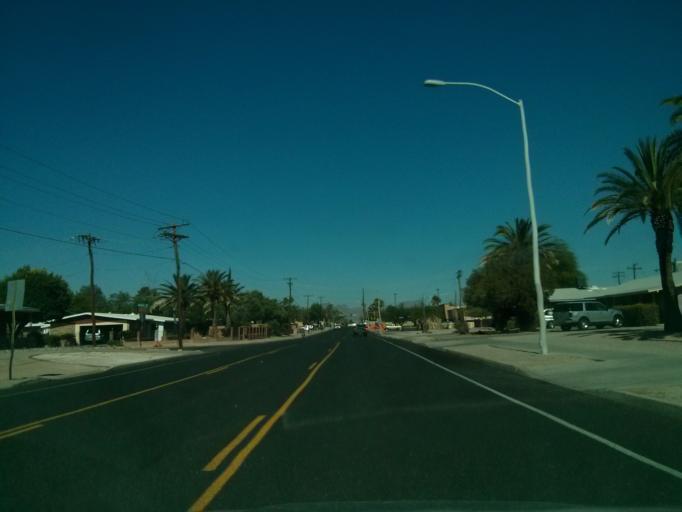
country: US
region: Arizona
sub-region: Pima County
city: Tucson
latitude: 32.2576
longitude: -110.9404
